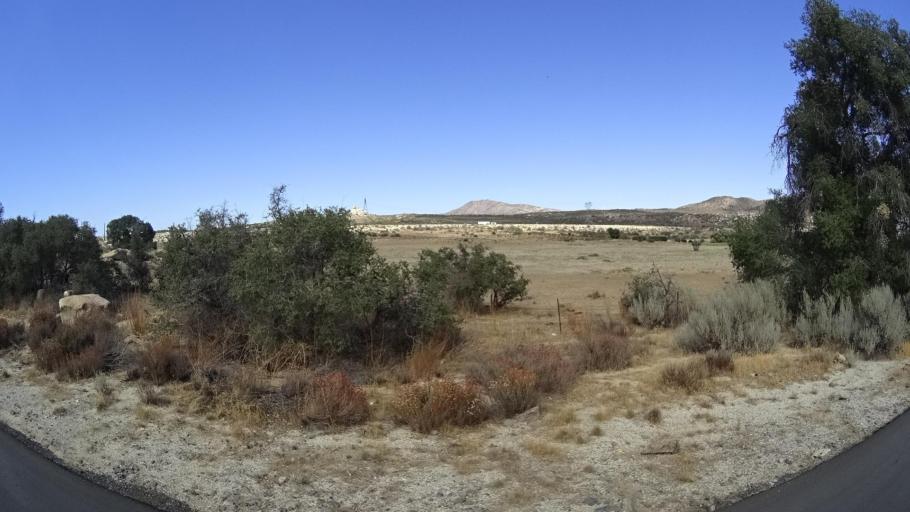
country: MX
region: Baja California
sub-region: Tecate
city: Cereso del Hongo
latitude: 32.6617
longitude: -116.2573
